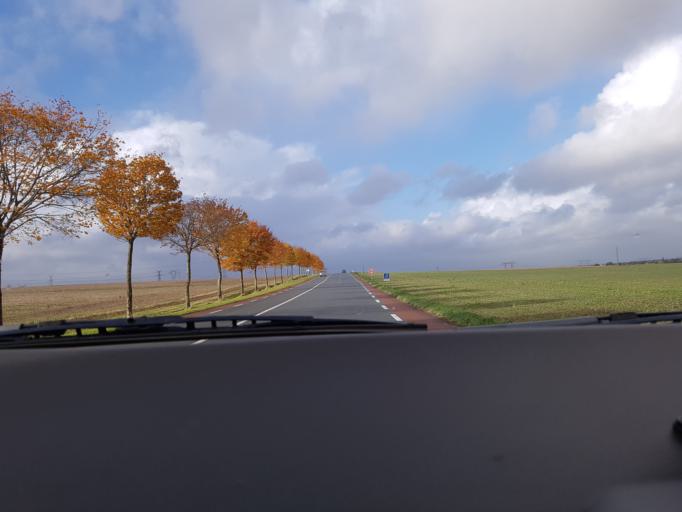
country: FR
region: Poitou-Charentes
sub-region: Departement de la Charente-Maritime
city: Les Gonds
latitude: 45.6622
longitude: -0.5941
